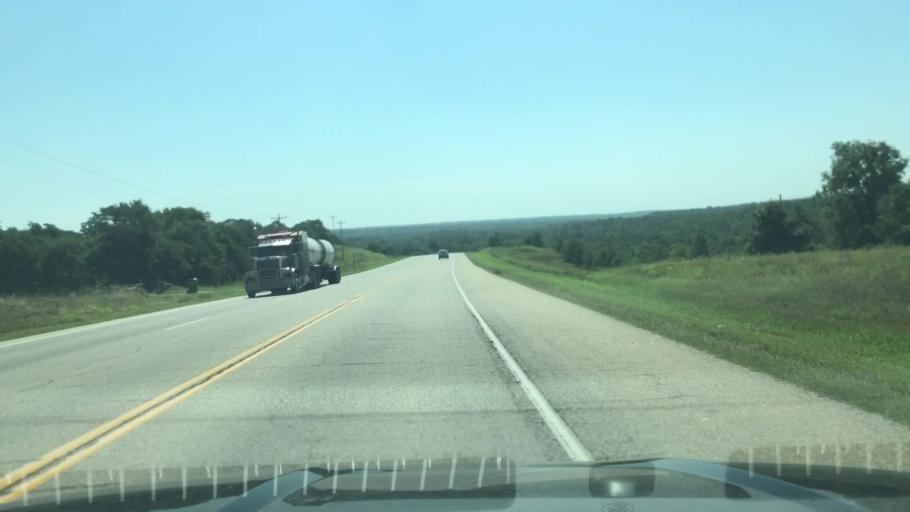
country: US
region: Oklahoma
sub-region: Creek County
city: Kellyville
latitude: 35.9881
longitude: -96.3342
